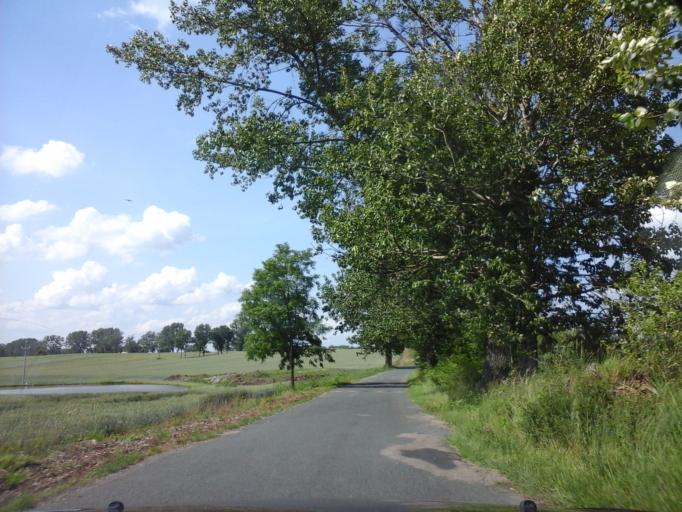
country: PL
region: West Pomeranian Voivodeship
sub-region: Powiat choszczenski
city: Choszczno
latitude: 53.1202
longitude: 15.3981
